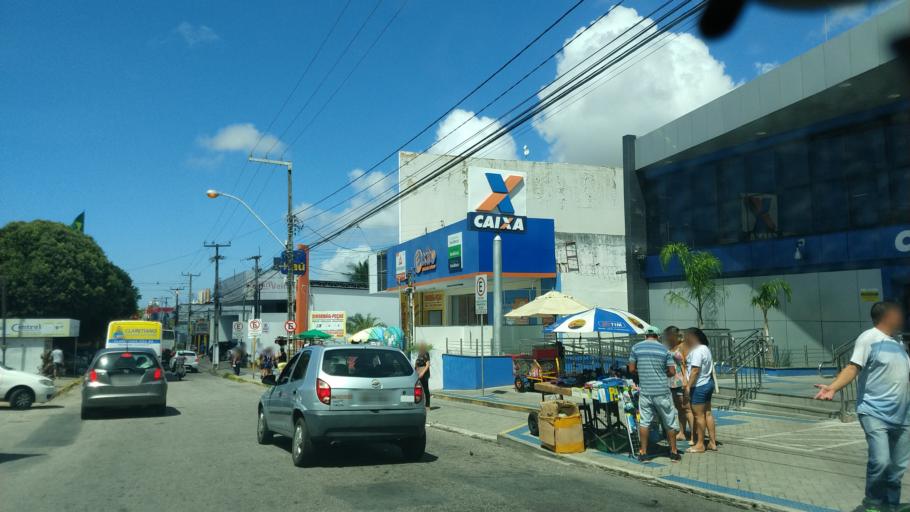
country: BR
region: Rio Grande do Norte
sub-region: Natal
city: Natal
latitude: -5.7998
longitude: -35.2163
